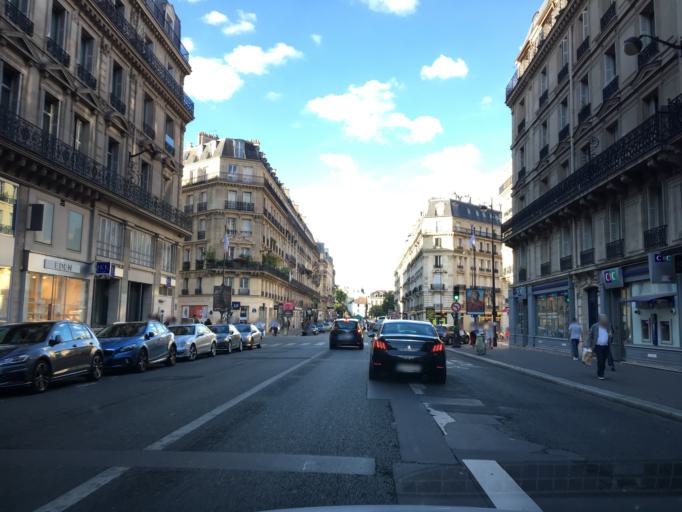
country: FR
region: Ile-de-France
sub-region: Paris
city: Paris
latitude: 48.8519
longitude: 2.3314
